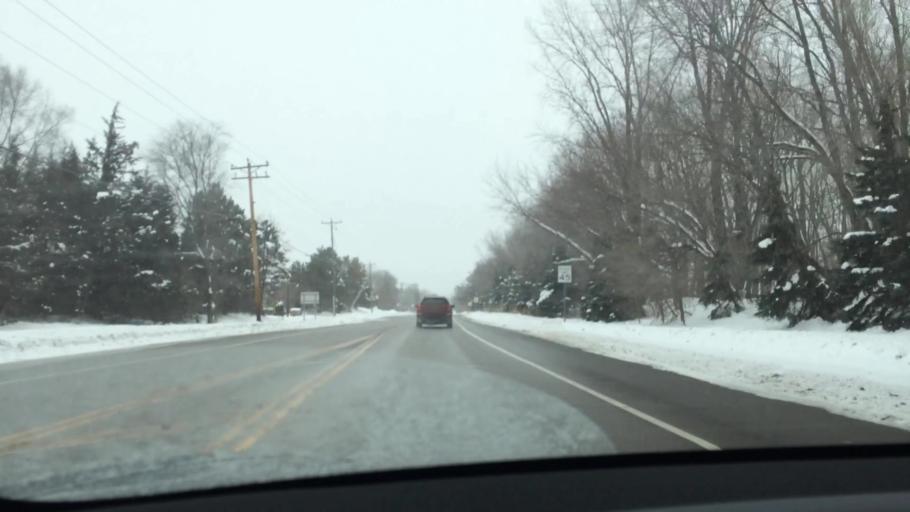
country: US
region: Minnesota
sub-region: Ramsey County
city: Shoreview
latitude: 45.1091
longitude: -93.1273
